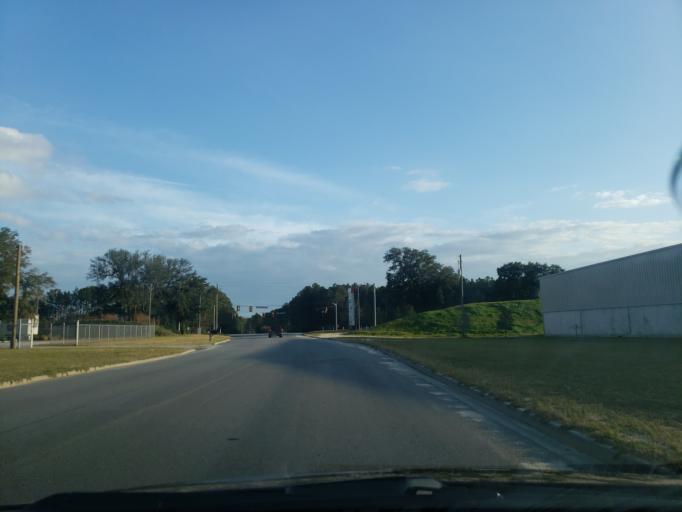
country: US
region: Georgia
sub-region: Chatham County
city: Bloomingdale
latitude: 32.1618
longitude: -81.2685
